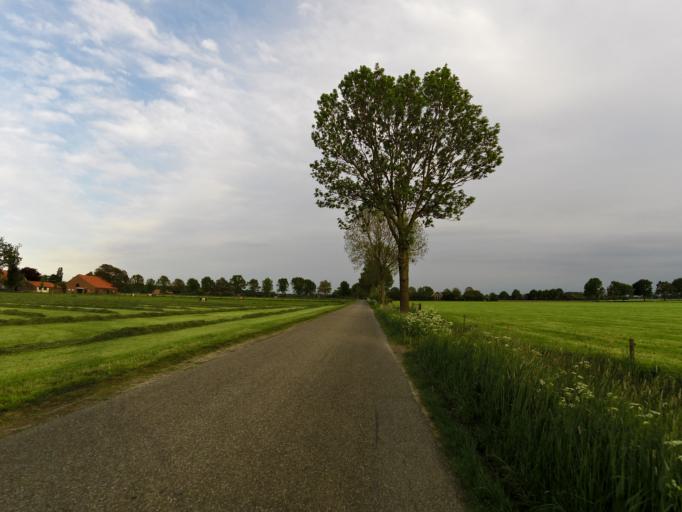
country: NL
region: Gelderland
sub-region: Oude IJsselstreek
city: Gendringen
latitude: 51.8568
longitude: 6.3816
